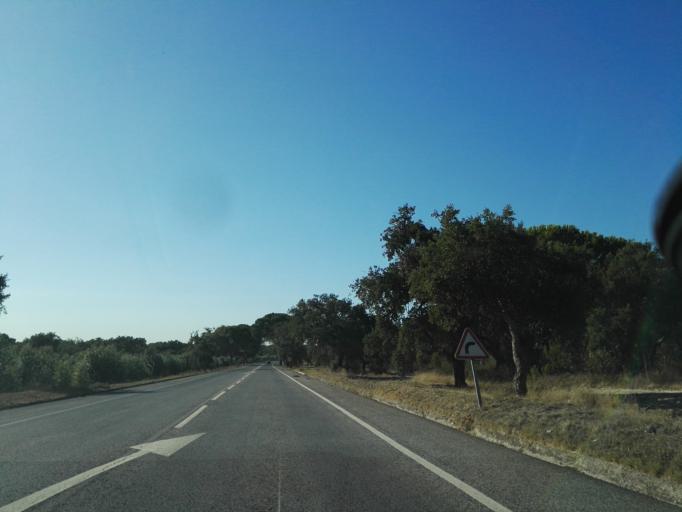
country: PT
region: Santarem
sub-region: Benavente
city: Poceirao
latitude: 38.8713
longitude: -8.7997
